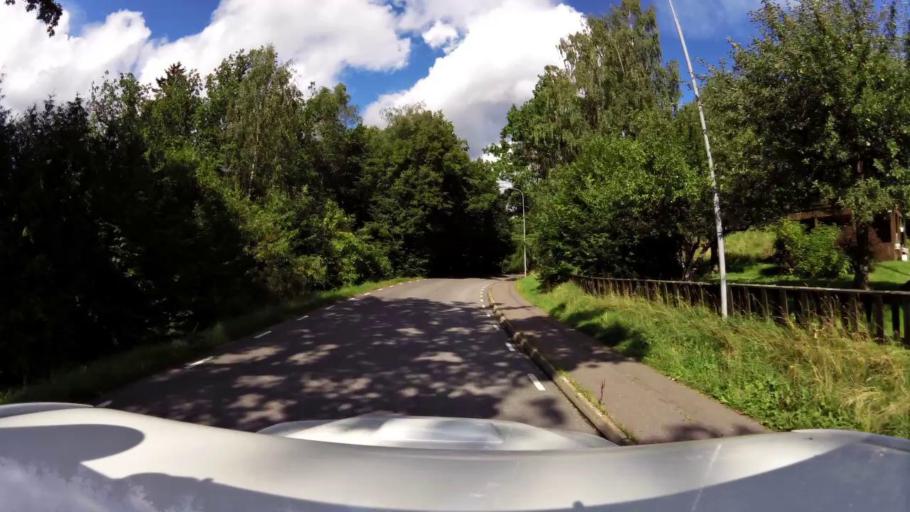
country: SE
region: OEstergoetland
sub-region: Kinda Kommun
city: Rimforsa
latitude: 58.2183
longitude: 15.6812
